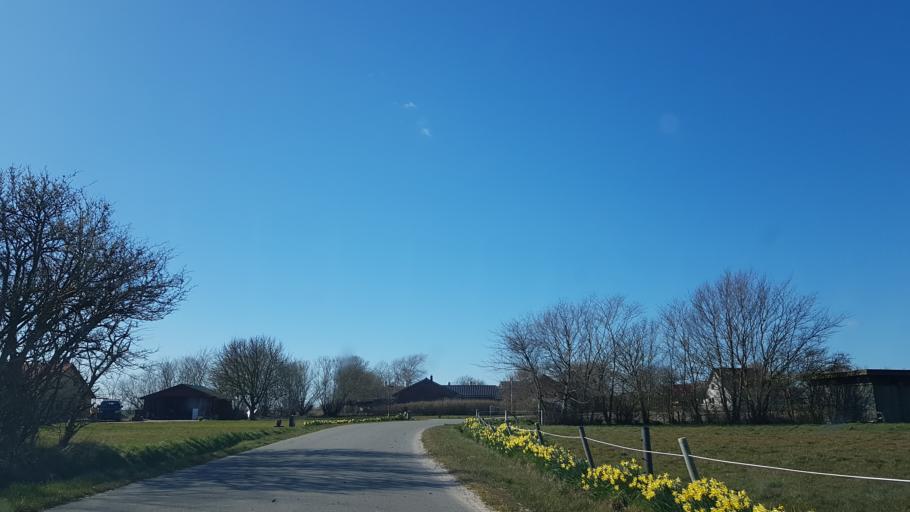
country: DK
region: South Denmark
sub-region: Esbjerg Kommune
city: Ribe
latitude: 55.2547
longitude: 8.6886
